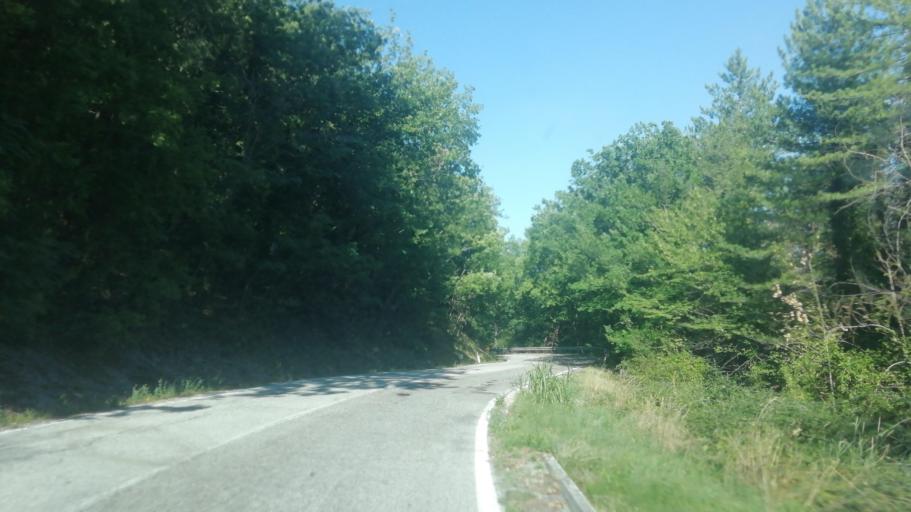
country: IT
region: The Marches
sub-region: Provincia di Pesaro e Urbino
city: Cagli
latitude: 43.5415
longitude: 12.6974
